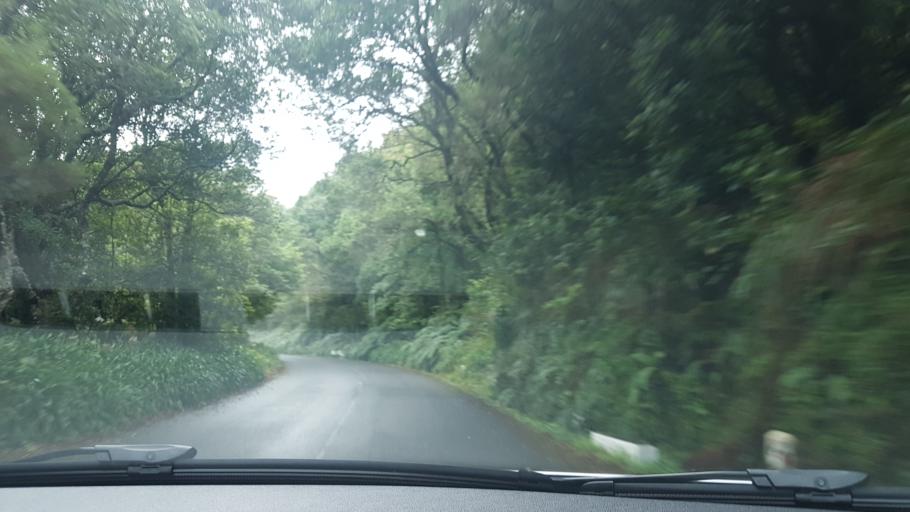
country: PT
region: Madeira
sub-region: Sao Vicente
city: Sao Vicente
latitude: 32.7548
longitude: -17.0161
